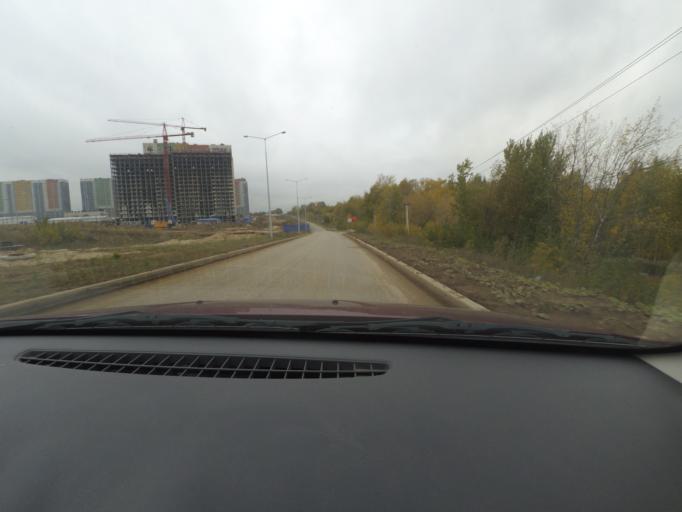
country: RU
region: Nizjnij Novgorod
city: Afonino
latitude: 56.2482
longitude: 44.0525
